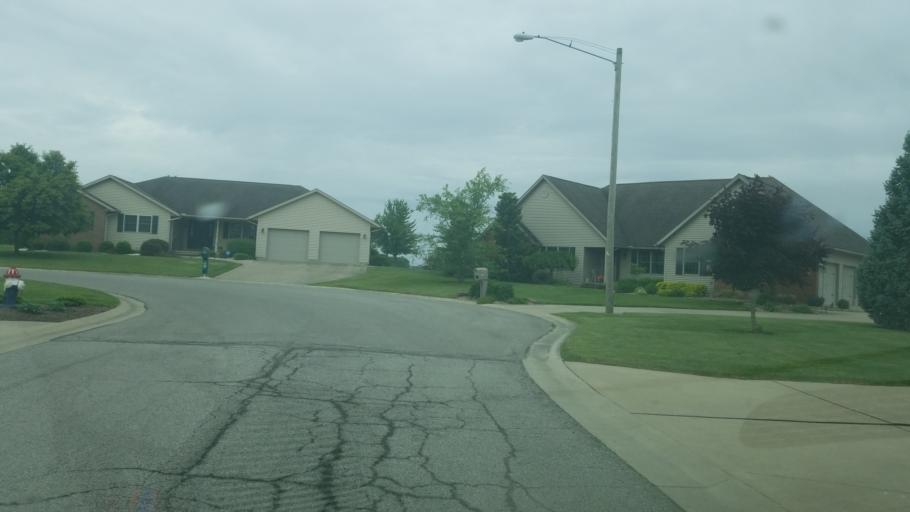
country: US
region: Ohio
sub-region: Crawford County
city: Bucyrus
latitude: 40.7937
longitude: -82.9930
